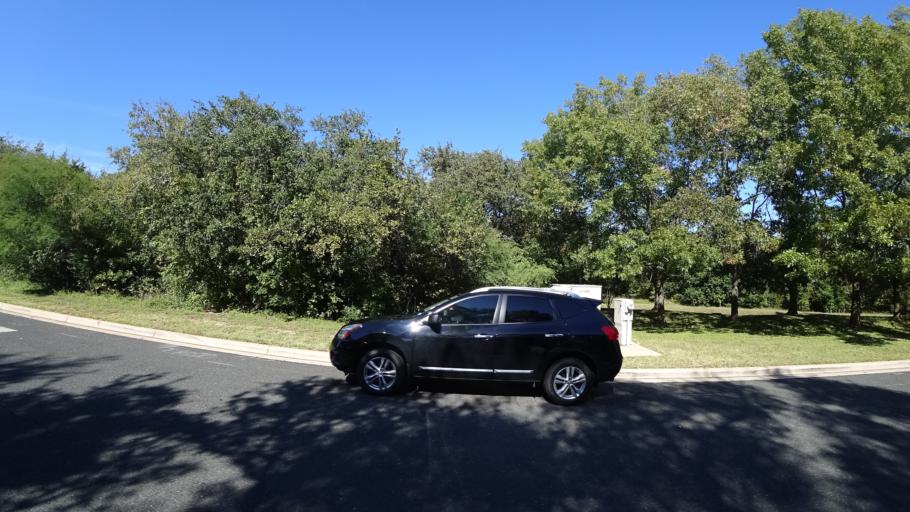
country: US
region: Texas
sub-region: Travis County
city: Shady Hollow
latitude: 30.2211
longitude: -97.8727
